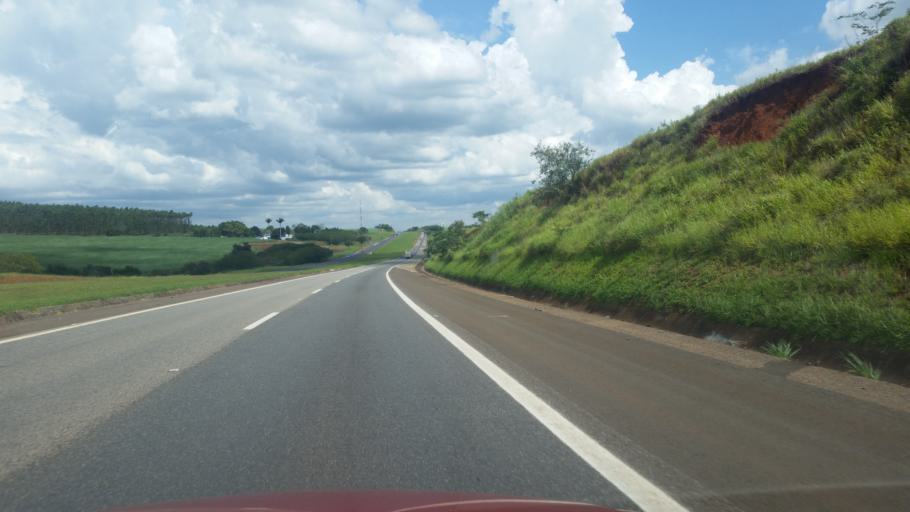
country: BR
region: Sao Paulo
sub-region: Tatui
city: Tatui
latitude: -23.2656
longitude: -47.8398
